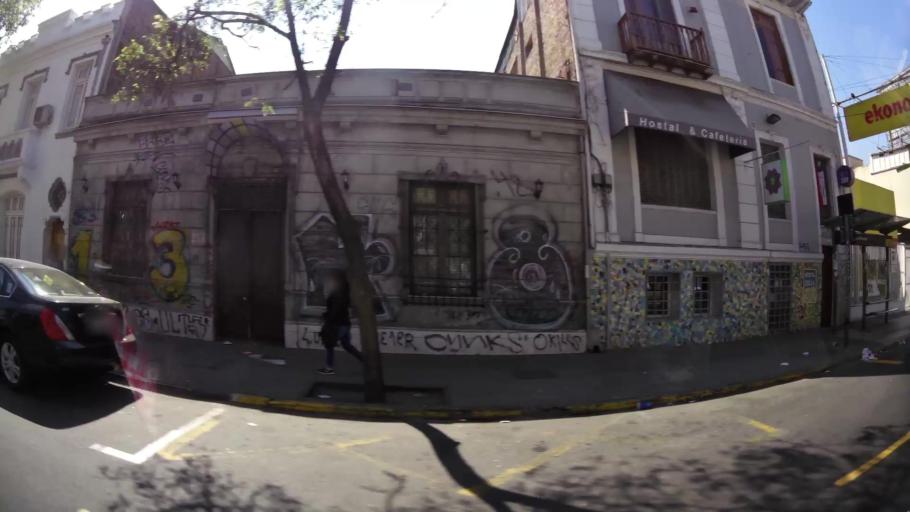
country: CL
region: Santiago Metropolitan
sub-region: Provincia de Santiago
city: Santiago
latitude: -33.4331
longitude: -70.6437
